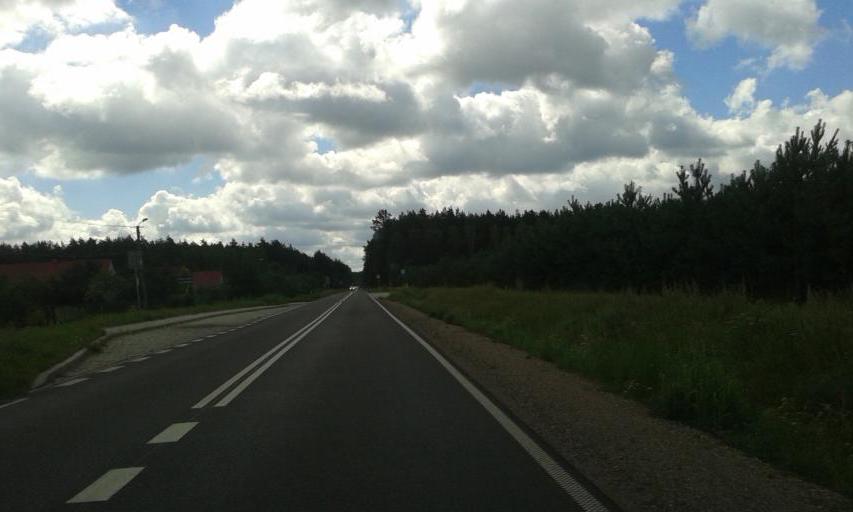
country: PL
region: West Pomeranian Voivodeship
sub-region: Powiat szczecinecki
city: Lubowo
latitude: 53.4746
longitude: 16.3577
